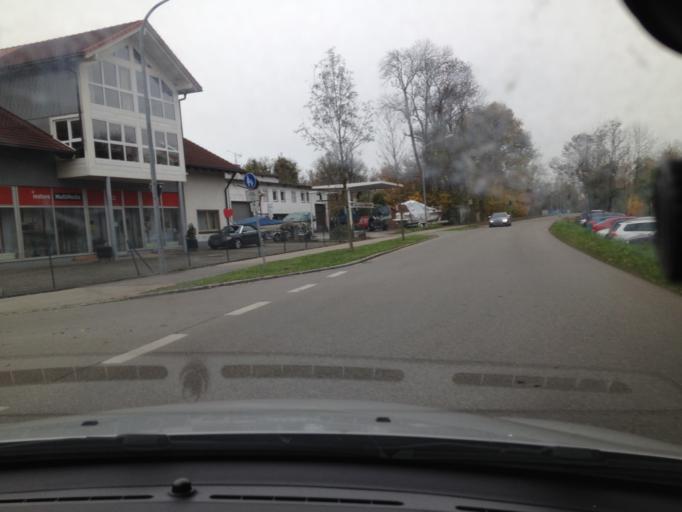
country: DE
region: Bavaria
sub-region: Swabia
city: Ettringen
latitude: 48.1089
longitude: 10.6673
